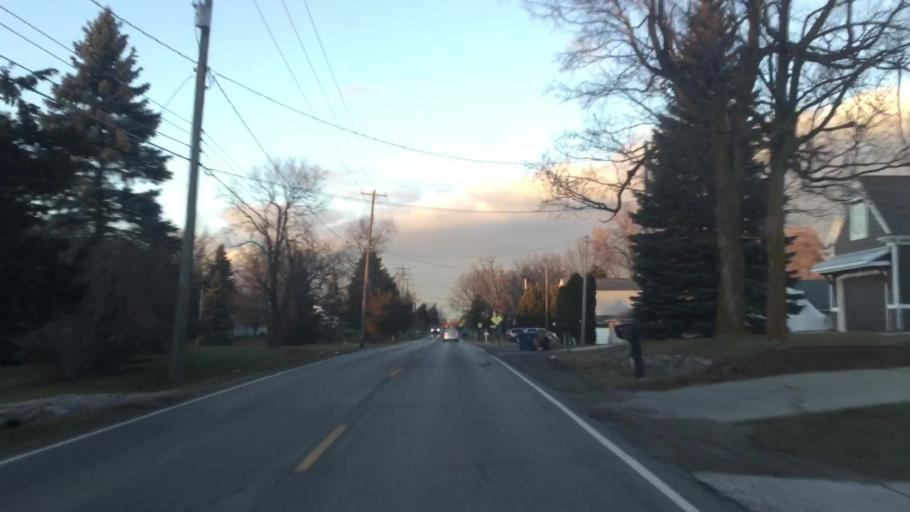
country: US
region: Michigan
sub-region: Genesee County
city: Lake Fenton
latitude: 42.8544
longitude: -83.7291
